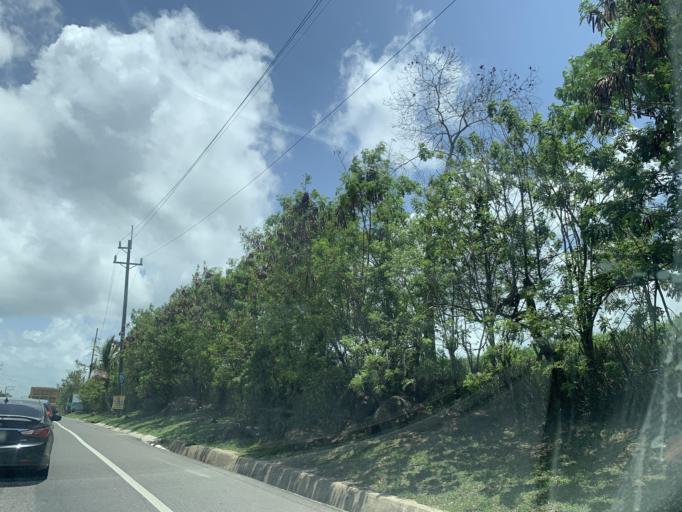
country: DO
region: Puerto Plata
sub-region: Puerto Plata
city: Puerto Plata
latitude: 19.7289
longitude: -70.6253
